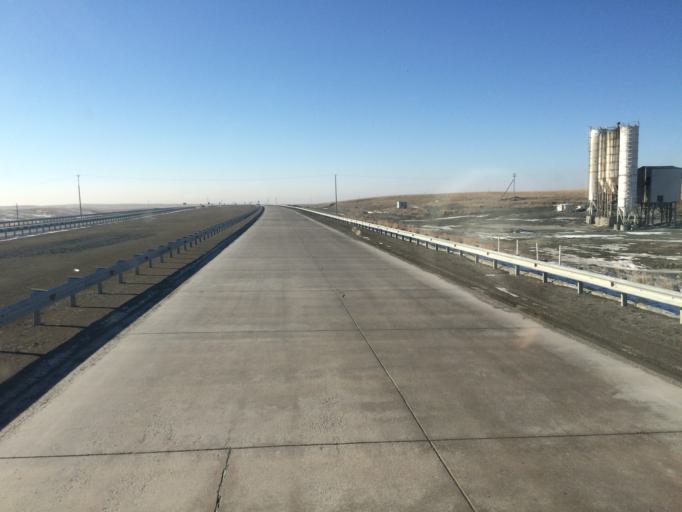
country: KZ
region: Zhambyl
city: Georgiyevka
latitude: 43.3549
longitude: 74.5691
